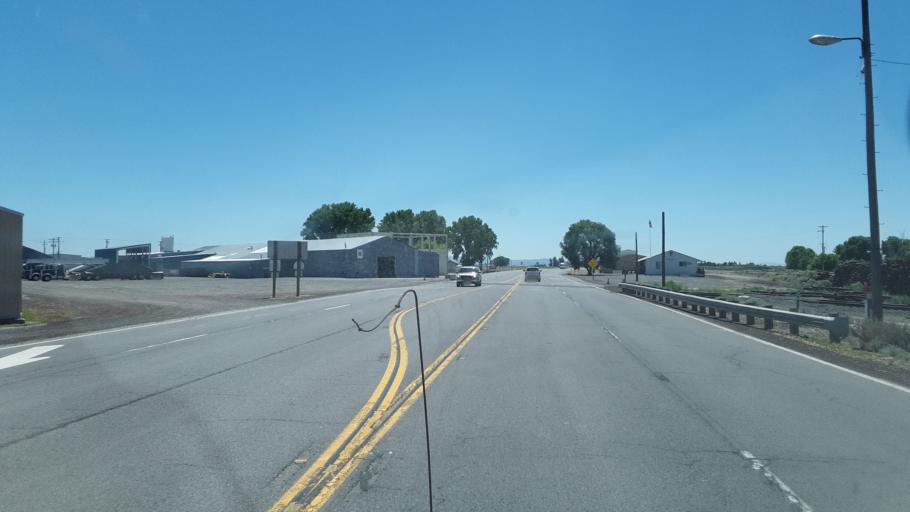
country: US
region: California
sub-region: Siskiyou County
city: Tulelake
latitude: 41.9979
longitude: -121.5190
